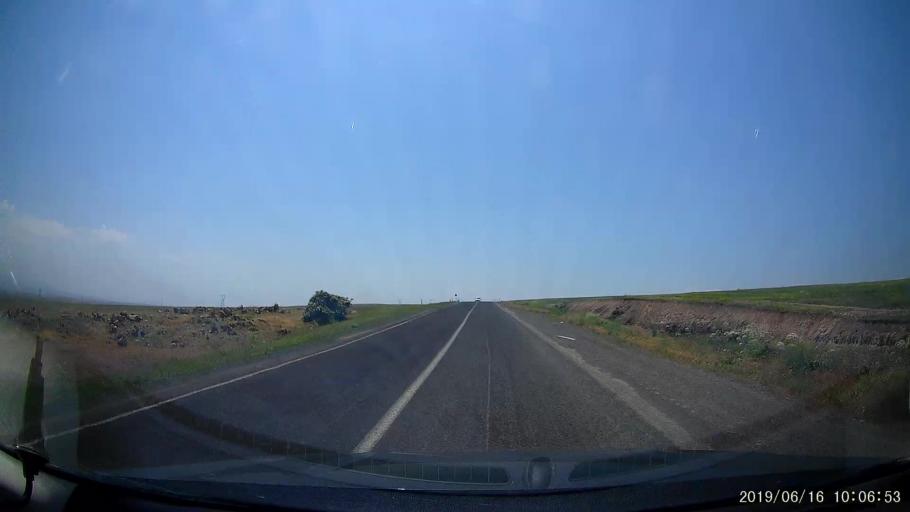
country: TR
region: Kars
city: Digor
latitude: 40.2500
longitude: 43.5483
